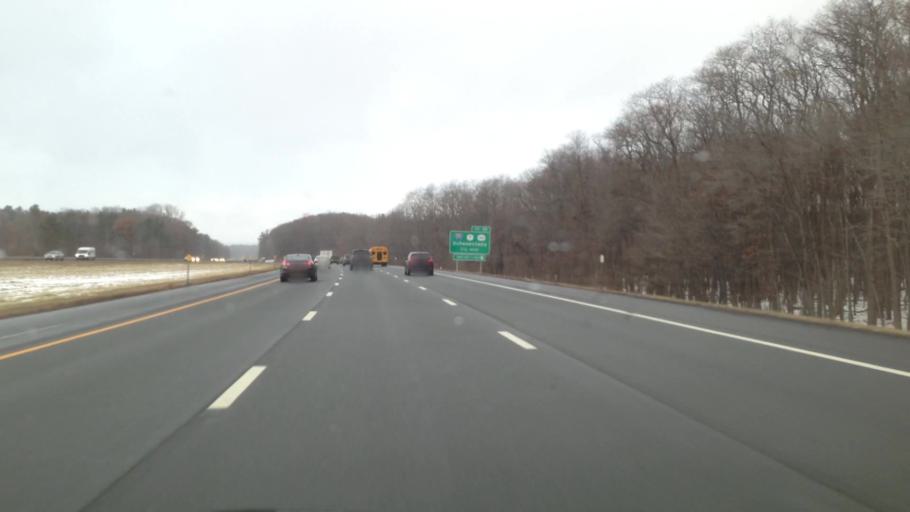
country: US
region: New York
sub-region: Albany County
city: Westmere
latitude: 42.7333
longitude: -73.8987
